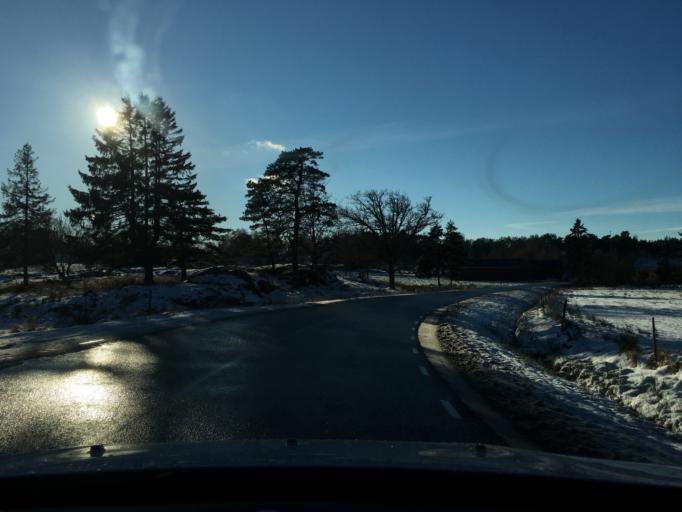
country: SE
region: Vaestra Goetaland
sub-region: Tjorns Kommun
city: Myggenas
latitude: 58.1240
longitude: 11.7451
